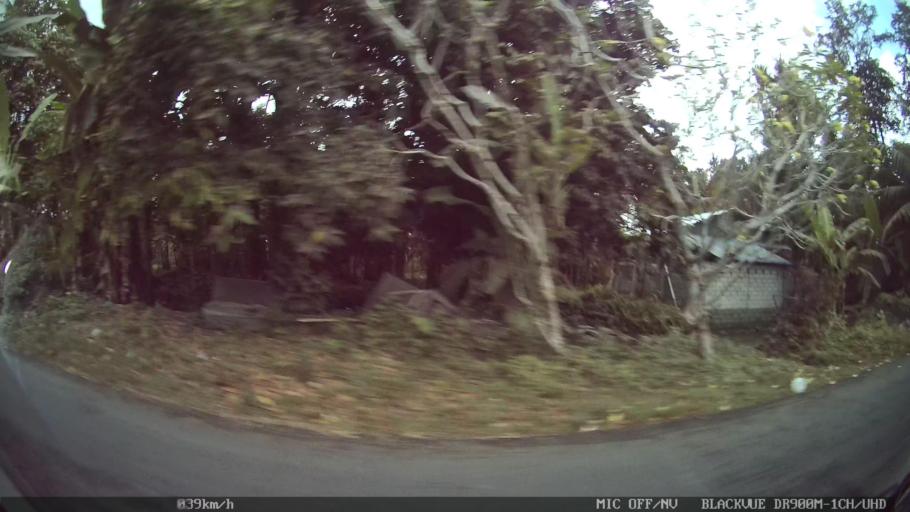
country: ID
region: Bali
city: Banjar Cemenggon
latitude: -8.5529
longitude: 115.1925
